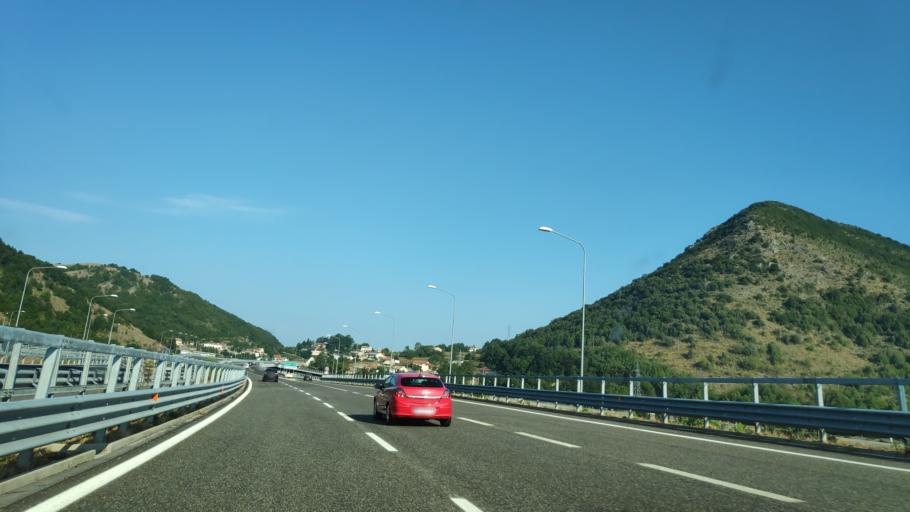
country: IT
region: Basilicate
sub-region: Provincia di Potenza
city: Lauria
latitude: 40.0171
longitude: 15.8913
